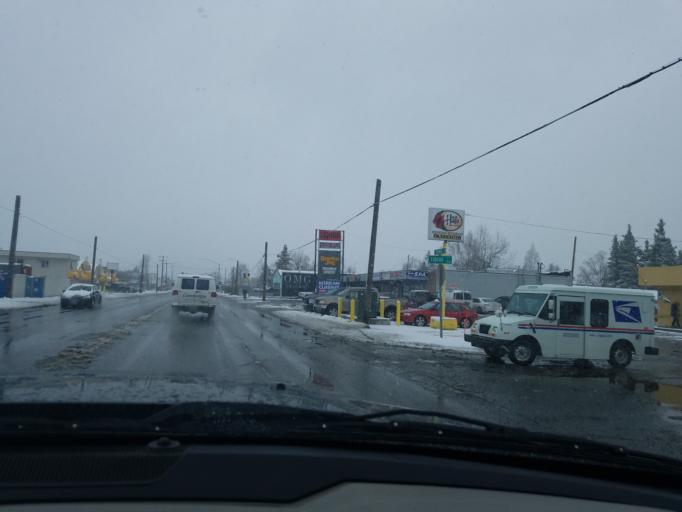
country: US
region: Alaska
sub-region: Anchorage Municipality
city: Anchorage
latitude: 61.1985
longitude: -149.8902
